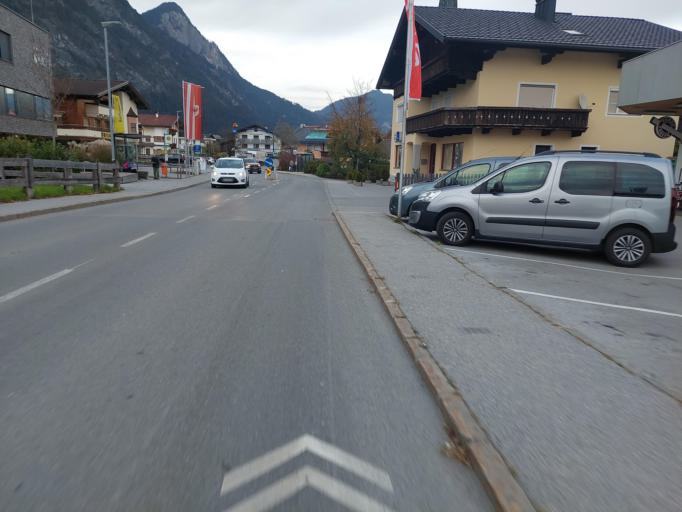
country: AT
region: Tyrol
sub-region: Politischer Bezirk Kufstein
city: Munster
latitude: 47.4202
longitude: 11.8330
